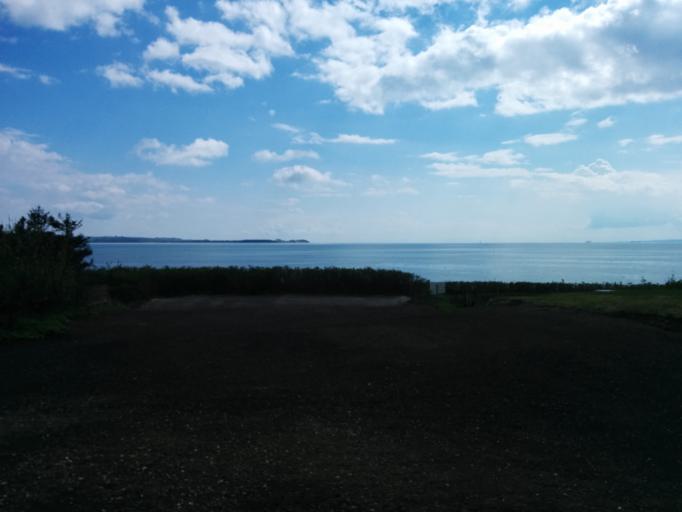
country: DK
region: Central Jutland
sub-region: Arhus Kommune
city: Logten
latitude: 56.2307
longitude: 10.3251
